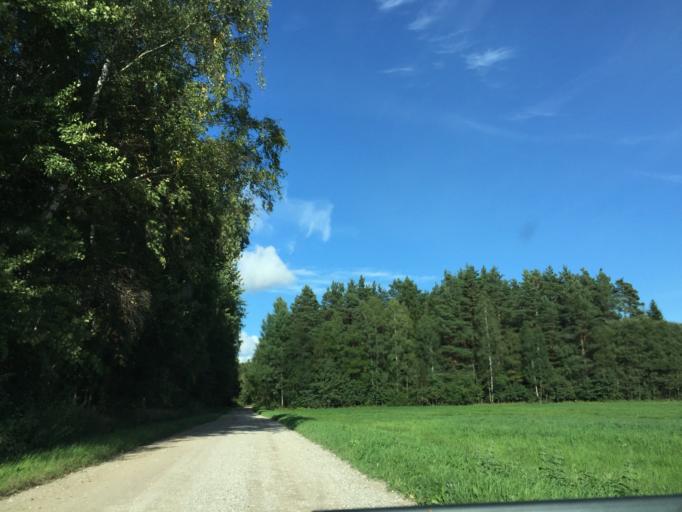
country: LV
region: Kuldigas Rajons
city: Kuldiga
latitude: 57.0016
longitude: 21.7734
